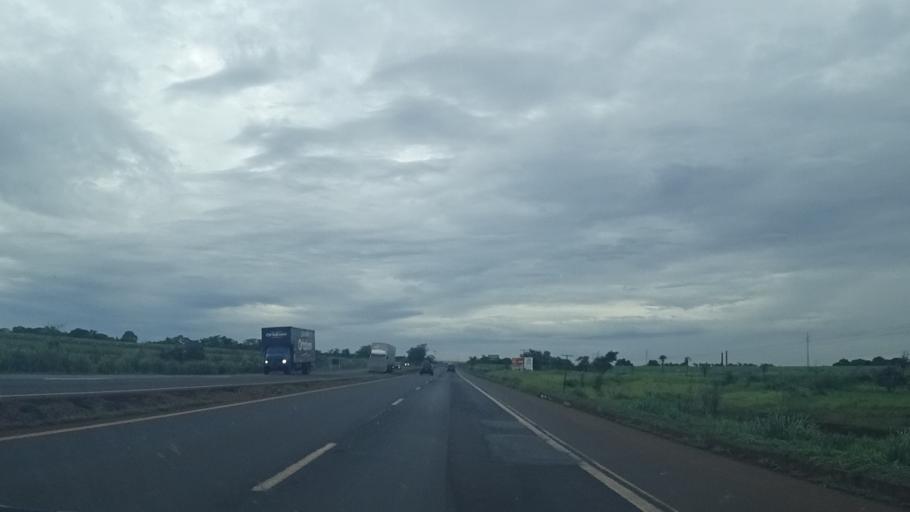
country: BR
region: Goias
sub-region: Itumbiara
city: Itumbiara
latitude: -18.4716
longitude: -49.1884
